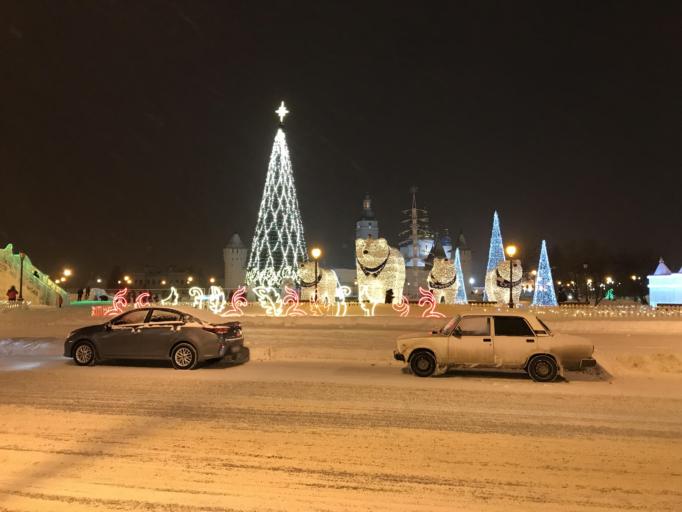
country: RU
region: Tjumen
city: Tobol'sk
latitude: 58.2014
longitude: 68.2541
